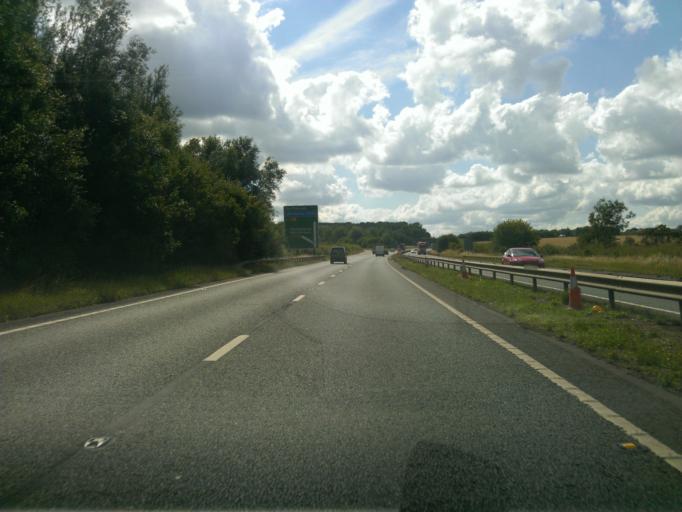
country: GB
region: England
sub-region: Northamptonshire
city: Brixworth
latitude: 52.4010
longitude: -0.9063
